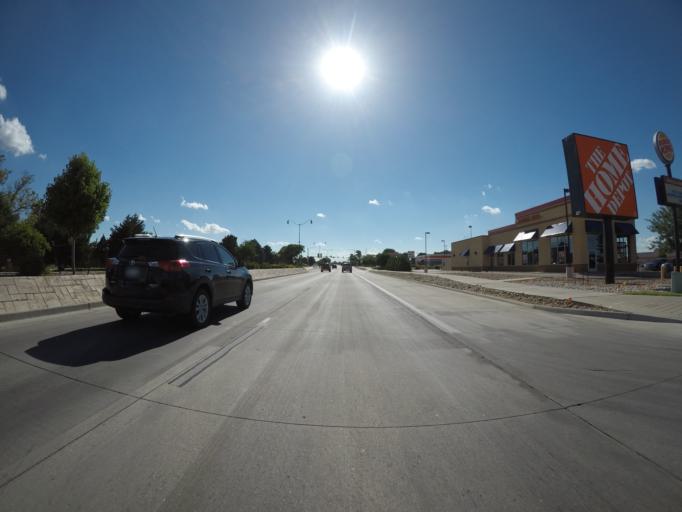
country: US
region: Colorado
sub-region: Logan County
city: Sterling
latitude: 40.6250
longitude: -103.2376
